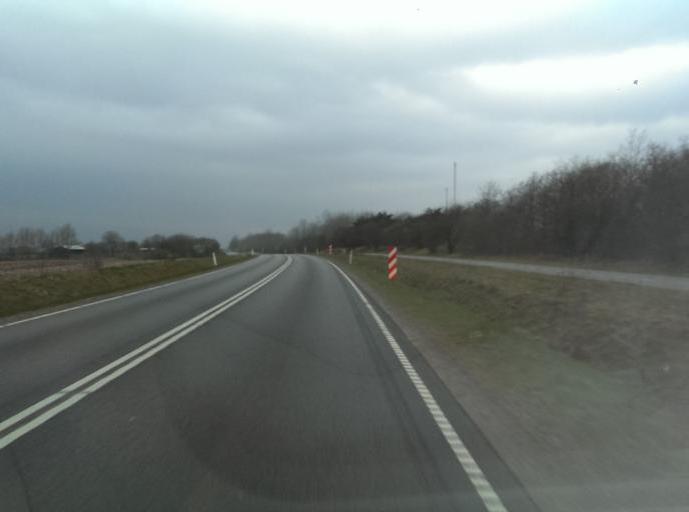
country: DK
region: South Denmark
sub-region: Esbjerg Kommune
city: Tjaereborg
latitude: 55.4670
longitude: 8.5284
